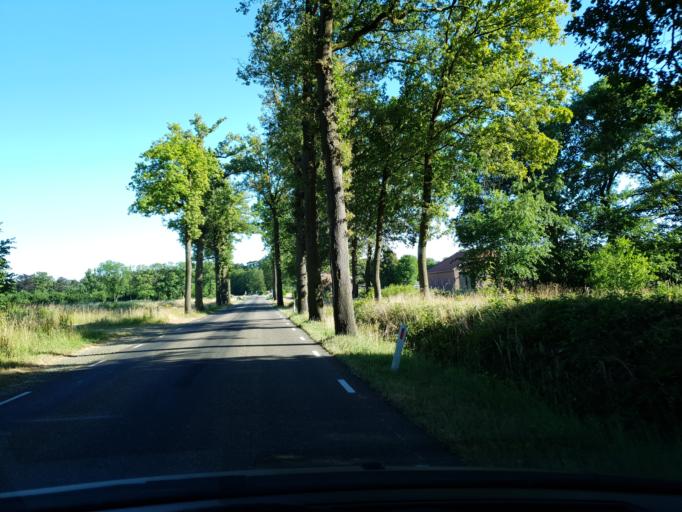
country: NL
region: North Brabant
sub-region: Gemeente Zundert
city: Zundert
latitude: 51.4899
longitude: 4.6078
